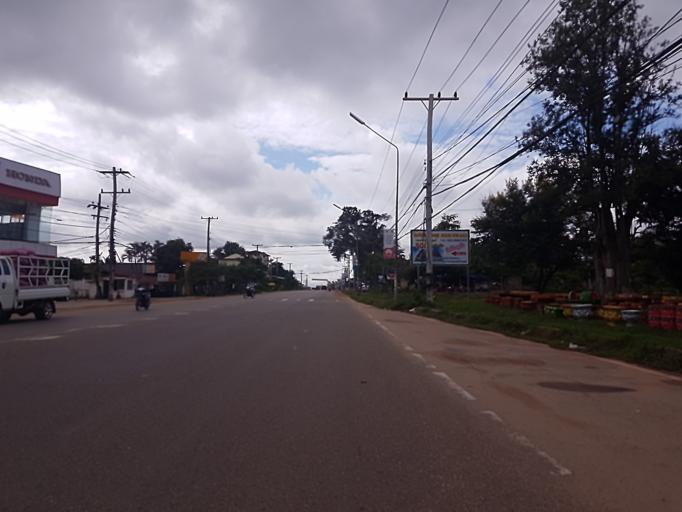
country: TH
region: Nong Khai
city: Tha Bo
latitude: 17.8922
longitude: 102.6452
